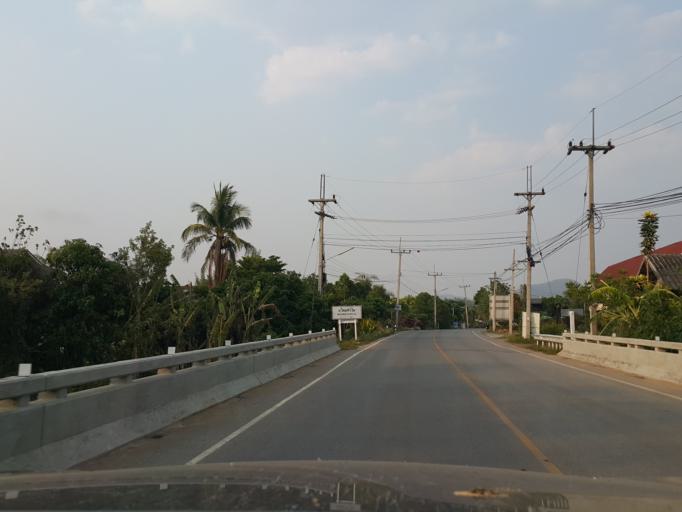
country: TH
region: Lamphun
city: Li
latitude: 17.8053
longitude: 98.9532
